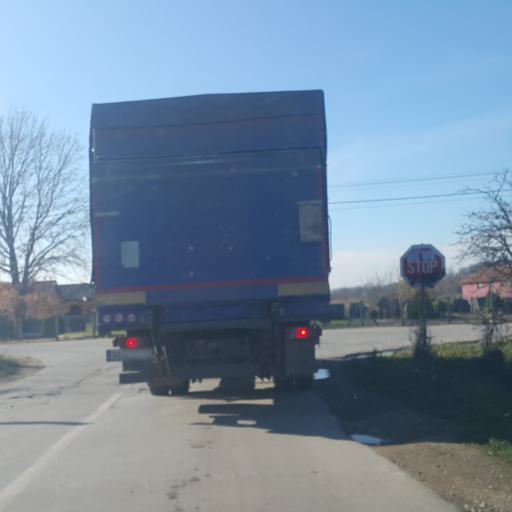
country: RS
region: Central Serbia
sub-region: Sumadijski Okrug
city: Lapovo
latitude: 44.2331
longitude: 21.0952
